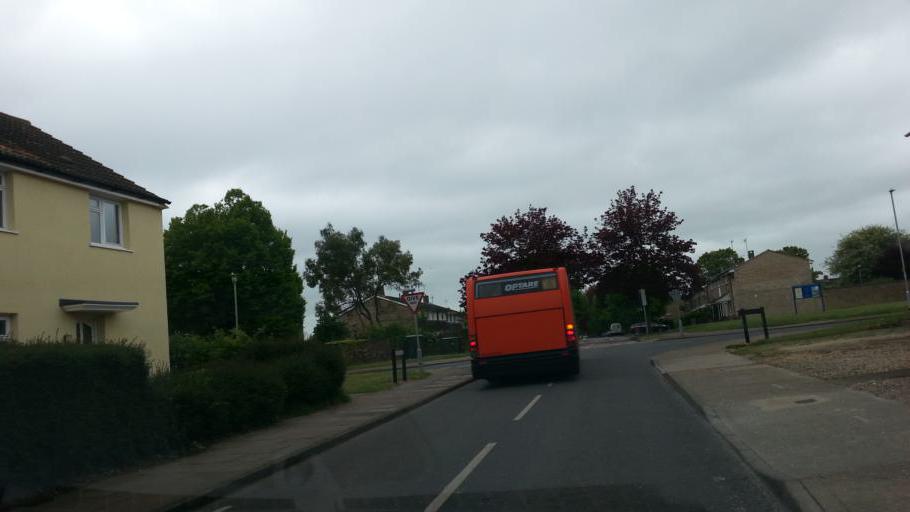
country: GB
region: England
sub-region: Suffolk
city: Bury St Edmunds
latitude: 52.2611
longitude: 0.6985
